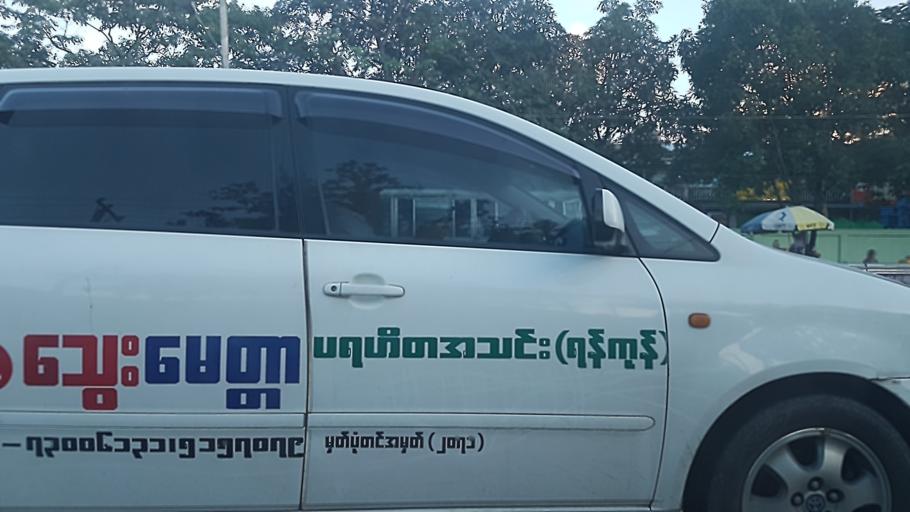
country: MM
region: Yangon
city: Yangon
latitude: 16.8938
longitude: 96.1204
